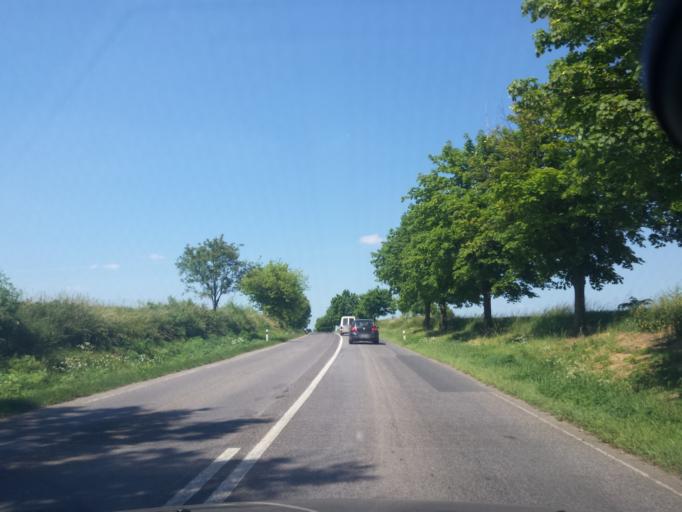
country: CZ
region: Central Bohemia
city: Velke Prilepy
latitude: 50.1685
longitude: 14.3162
